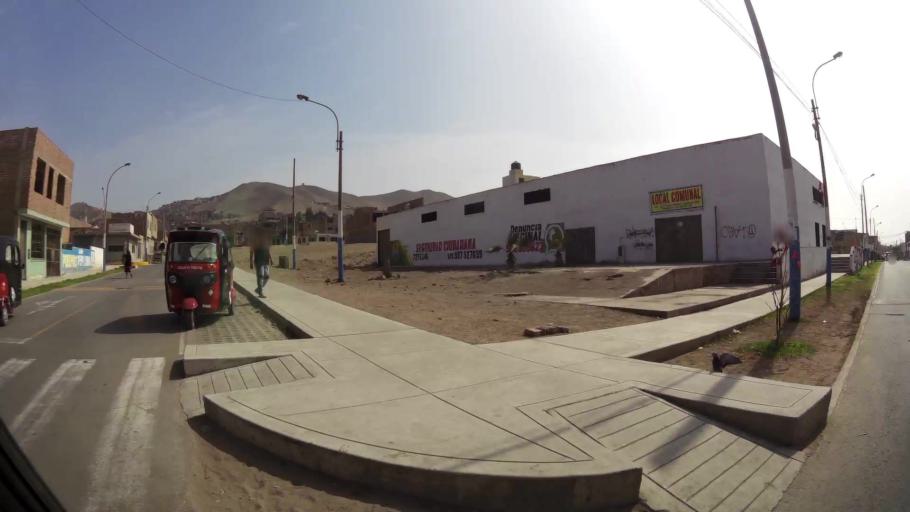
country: PE
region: Lima
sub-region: Lima
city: Santa Rosa
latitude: -11.7813
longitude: -77.1612
